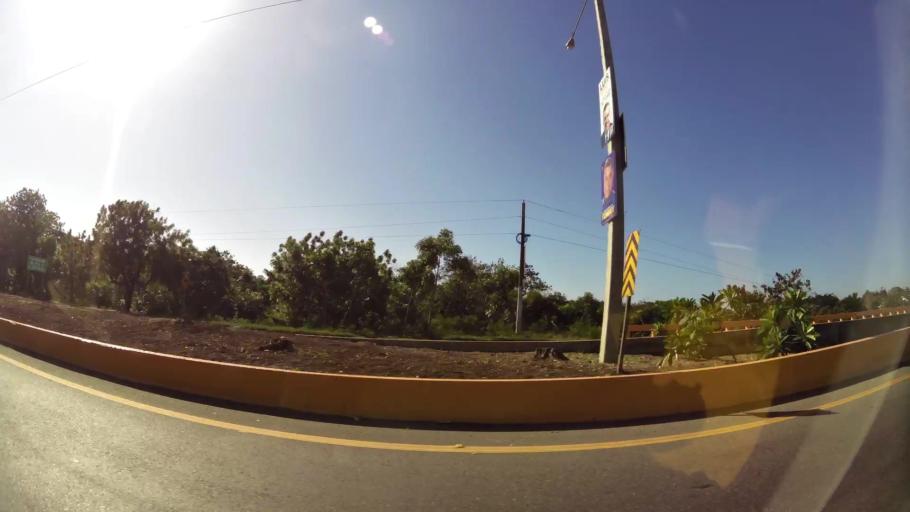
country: DO
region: San Cristobal
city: El Carril
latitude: 18.4398
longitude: -70.0063
